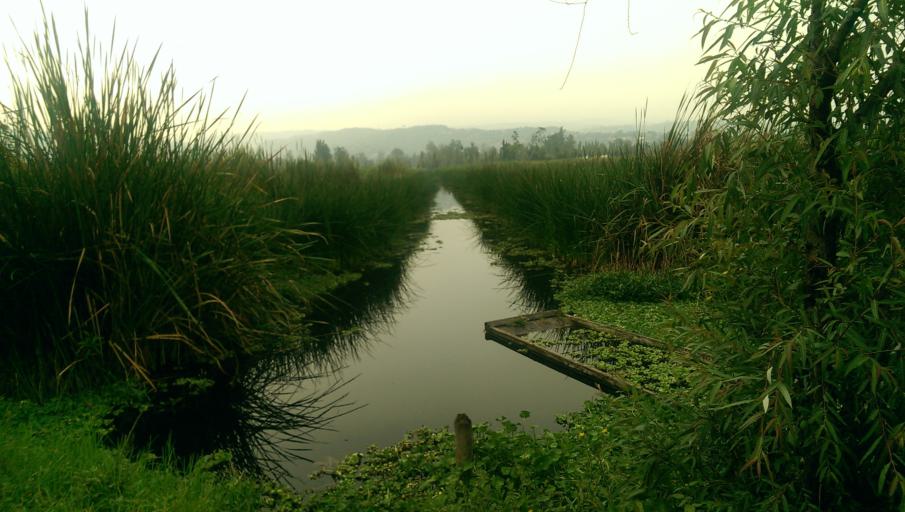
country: MX
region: Mexico City
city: Xochimilco
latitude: 19.2663
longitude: -99.0542
